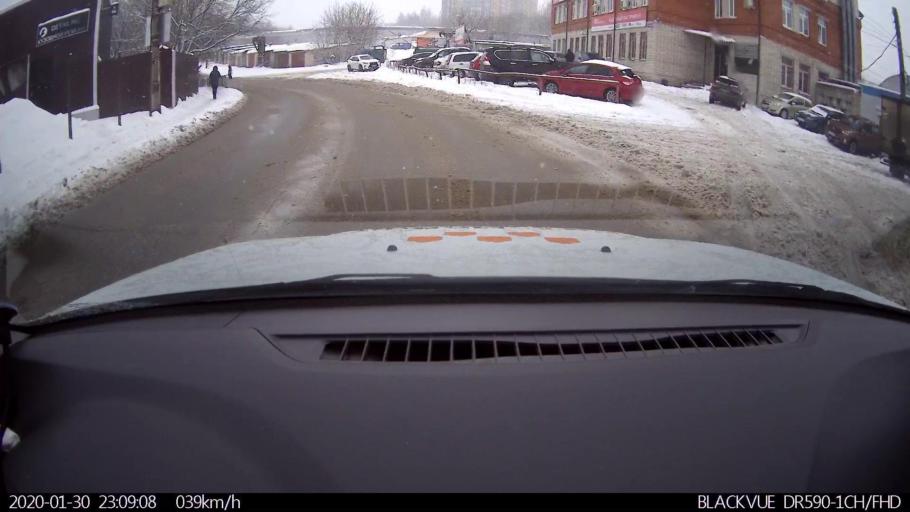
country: RU
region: Nizjnij Novgorod
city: Bor
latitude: 56.3130
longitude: 44.0567
